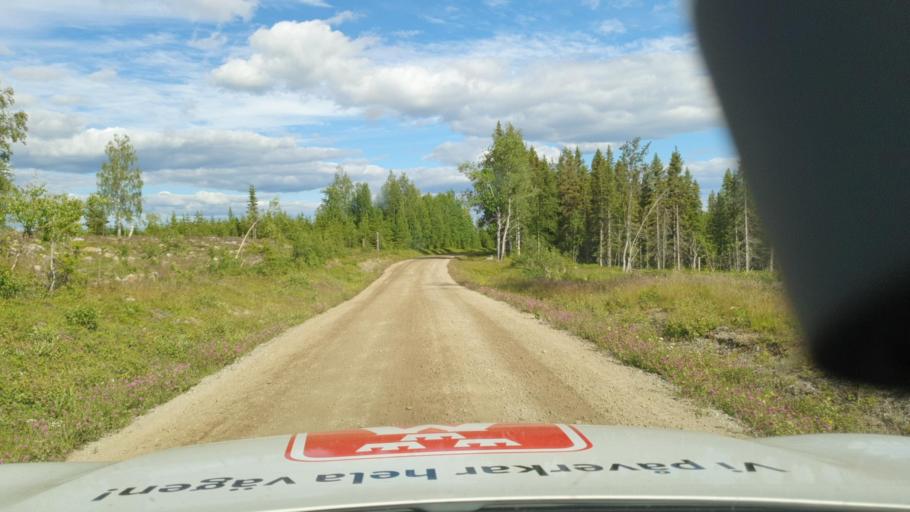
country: SE
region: Vaesterbotten
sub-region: Lycksele Kommun
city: Lycksele
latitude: 64.3304
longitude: 18.3753
